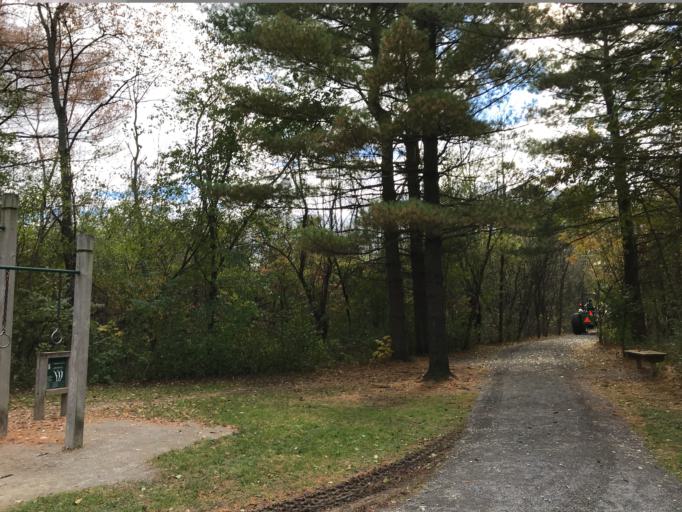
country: US
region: Michigan
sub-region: Washtenaw County
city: Ann Arbor
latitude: 42.2561
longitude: -83.7097
